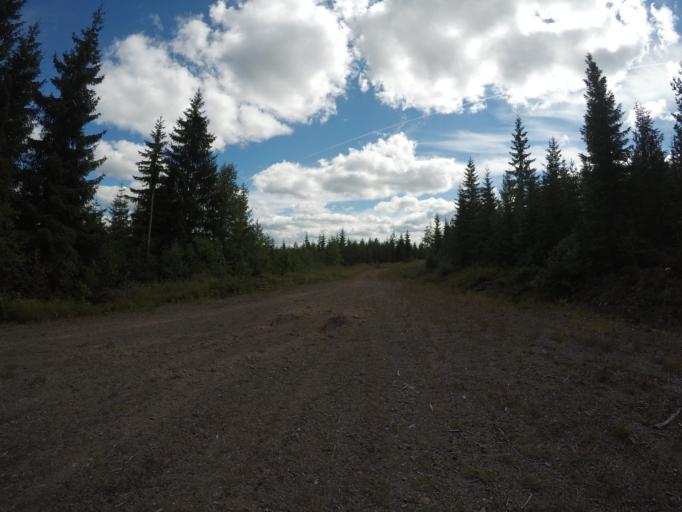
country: SE
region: Vaermland
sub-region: Filipstads Kommun
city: Lesjofors
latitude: 60.0814
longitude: 14.4591
